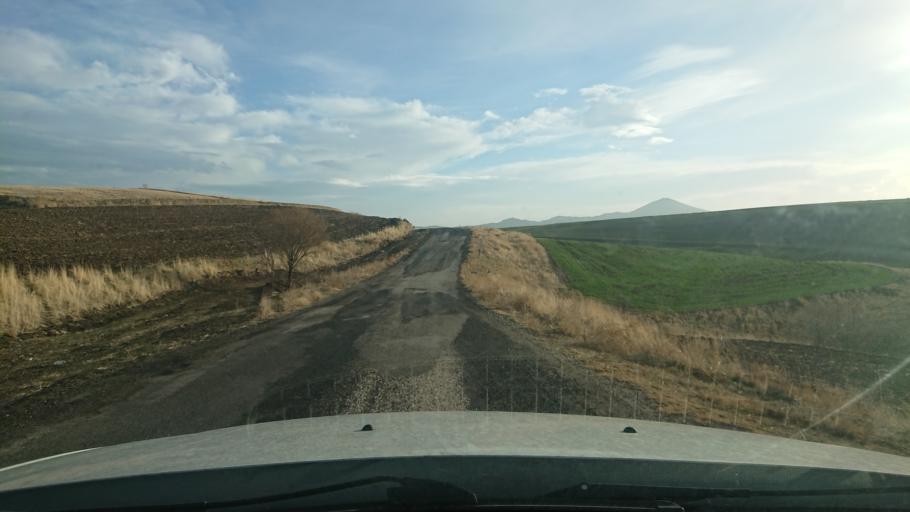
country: TR
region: Aksaray
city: Acipinar
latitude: 38.6665
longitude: 33.8516
